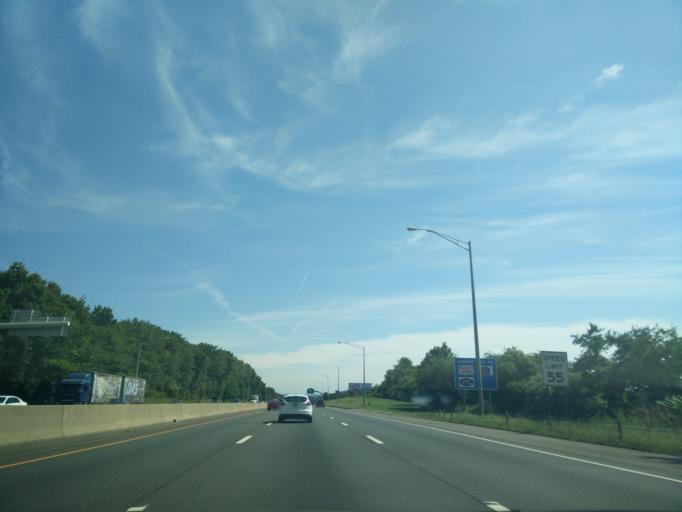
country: US
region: Connecticut
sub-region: New Haven County
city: Woodmont
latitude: 41.2634
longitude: -72.9838
